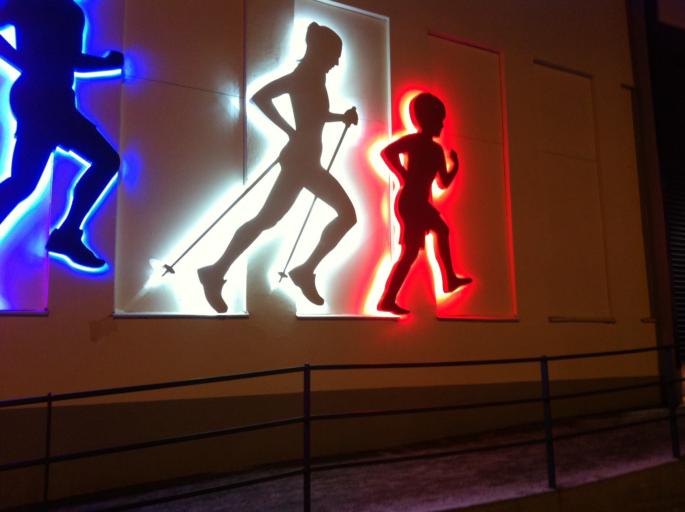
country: SE
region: Stockholm
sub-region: Stockholms Kommun
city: Bromma
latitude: 59.3571
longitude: 17.9488
